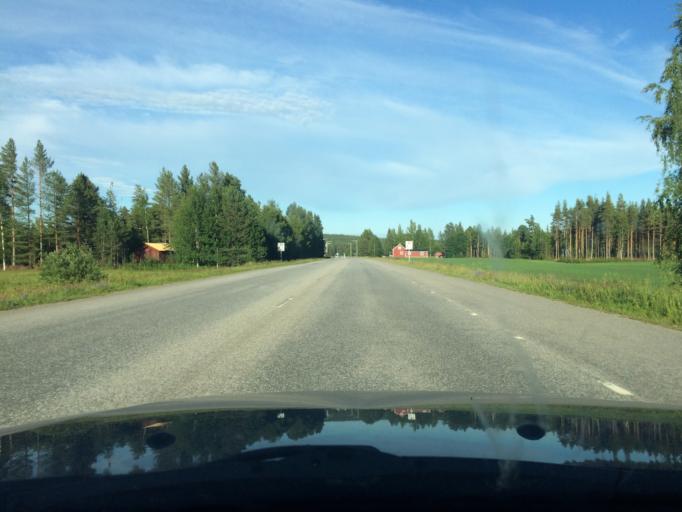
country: SE
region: Norrbotten
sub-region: Pitea Kommun
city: Bergsviken
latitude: 65.3149
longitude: 21.3222
